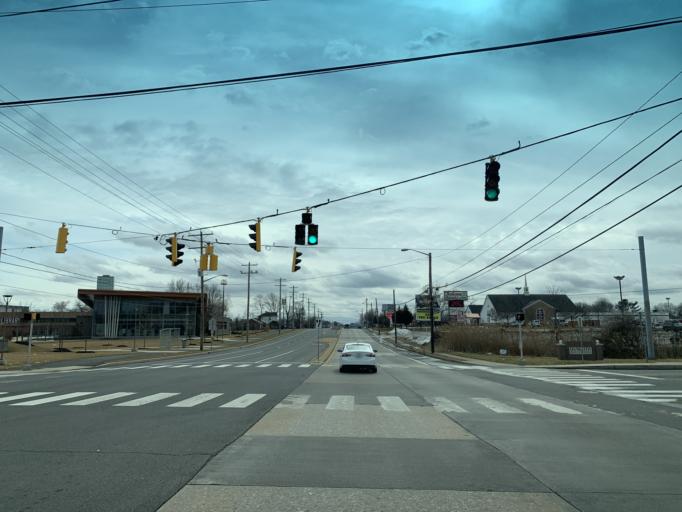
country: US
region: Delaware
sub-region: New Castle County
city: Wilmington Manor
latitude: 39.7031
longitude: -75.5513
